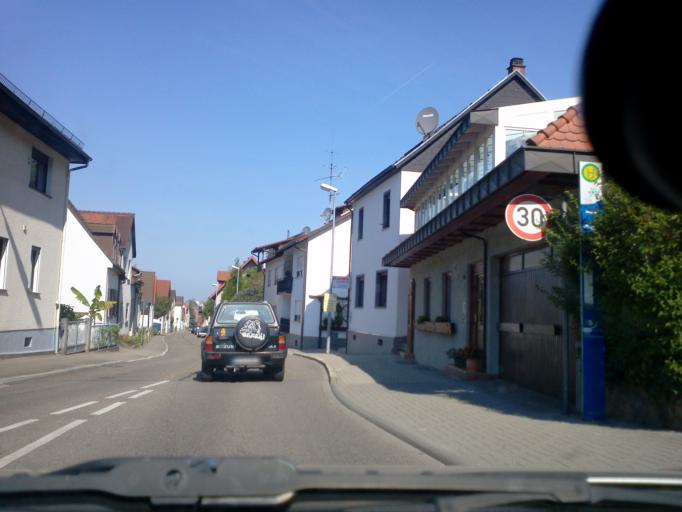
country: DE
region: Baden-Wuerttemberg
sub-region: Karlsruhe Region
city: Weingarten
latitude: 49.0841
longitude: 8.5604
